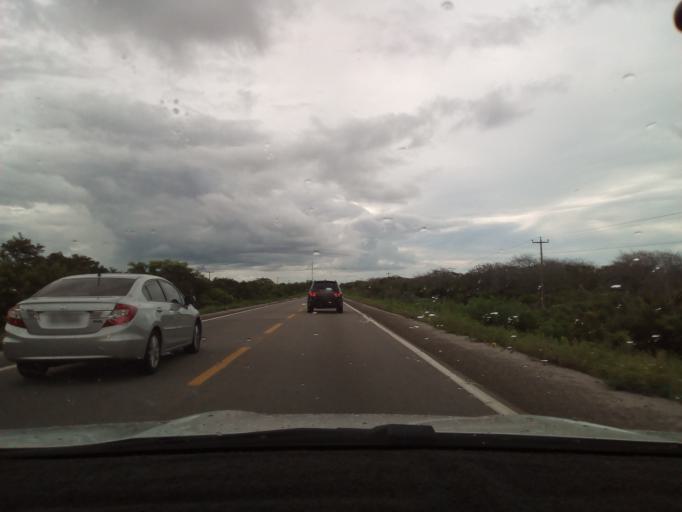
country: BR
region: Ceara
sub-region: Jaguaruana
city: Jaguaruana
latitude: -4.7529
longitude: -37.5297
